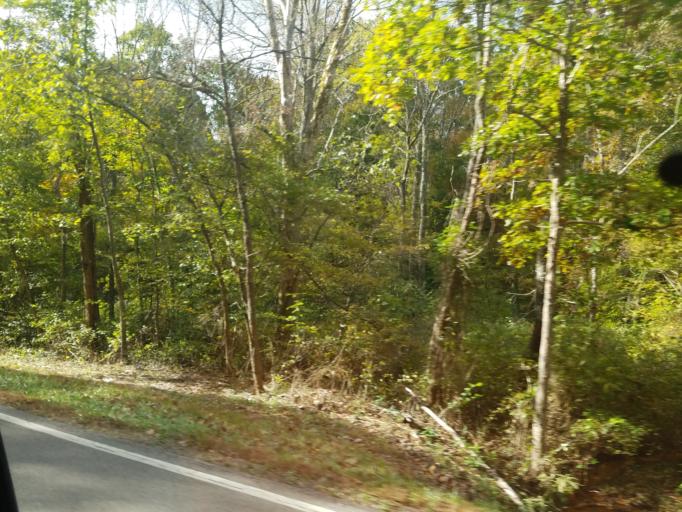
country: US
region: Ohio
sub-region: Vinton County
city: McArthur
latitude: 39.1691
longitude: -82.4390
